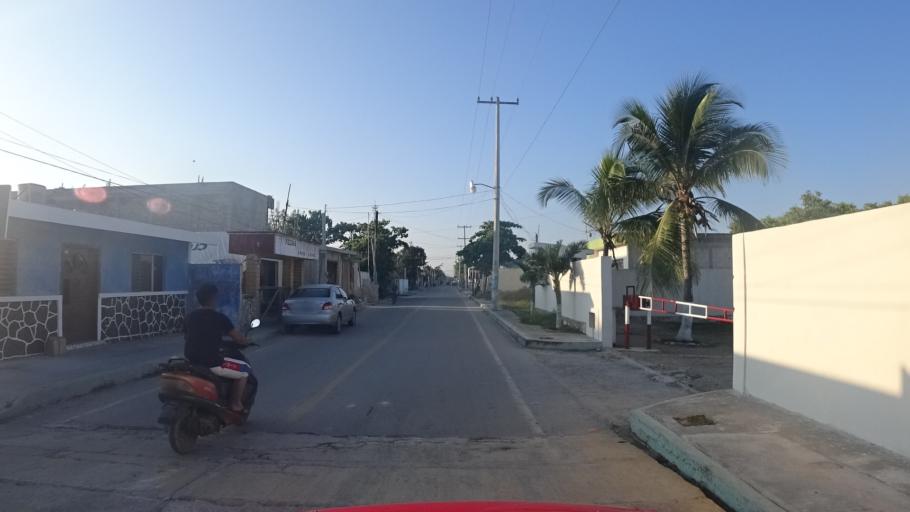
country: MX
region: Yucatan
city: Rio Lagartos
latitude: 21.5941
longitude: -88.1576
